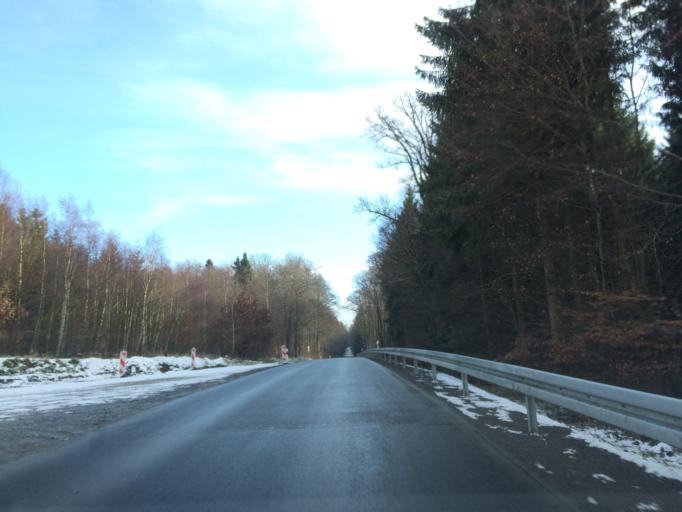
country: DE
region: Hesse
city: Bad Camberg
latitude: 50.3227
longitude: 8.3311
